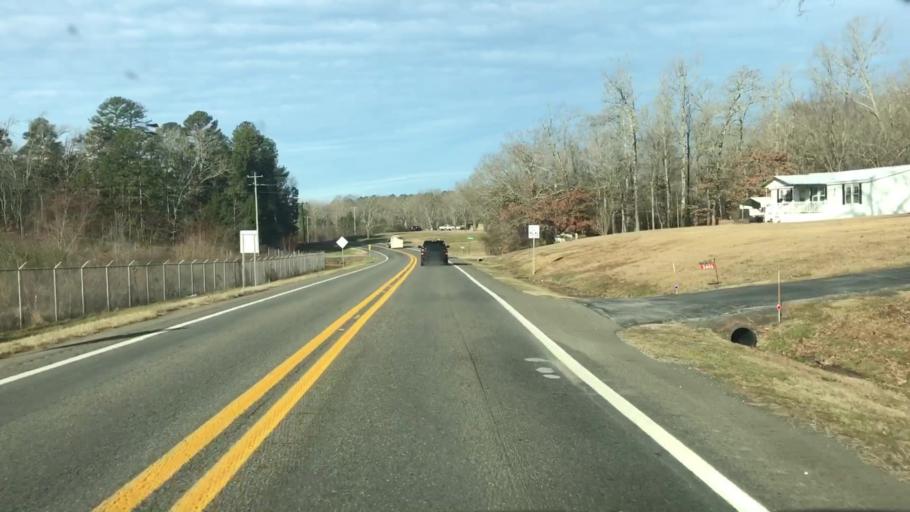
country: US
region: Arkansas
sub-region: Montgomery County
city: Mount Ida
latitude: 34.5312
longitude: -93.5314
